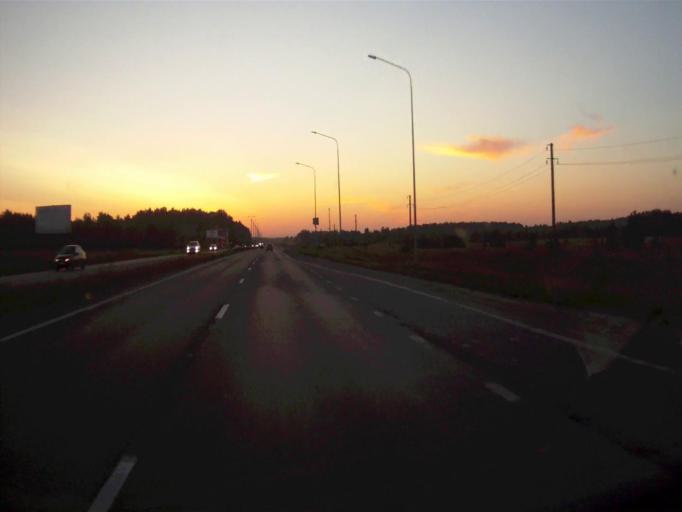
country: RU
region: Chelyabinsk
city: Roshchino
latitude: 55.1894
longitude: 61.2326
